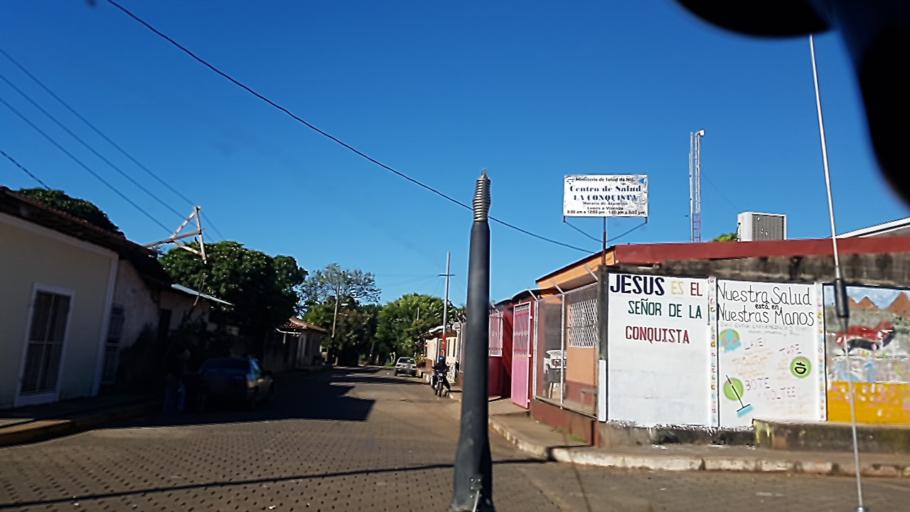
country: NI
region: Carazo
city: Santa Teresa
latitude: 11.7341
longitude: -86.1932
